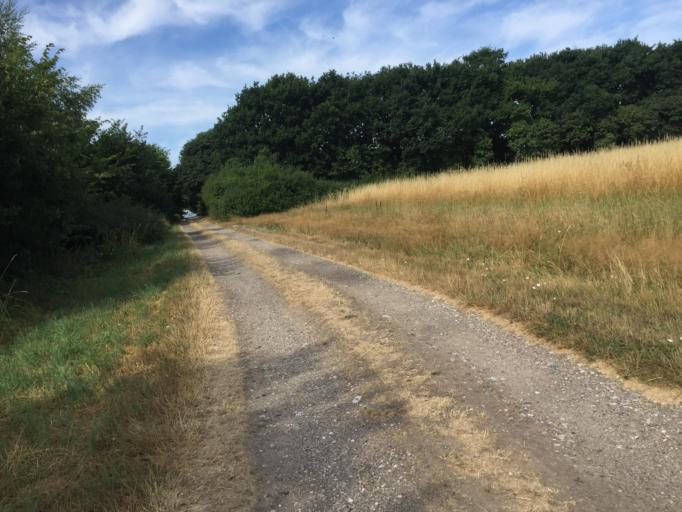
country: DK
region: Central Jutland
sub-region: Arhus Kommune
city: Beder
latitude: 55.9586
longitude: 10.4101
